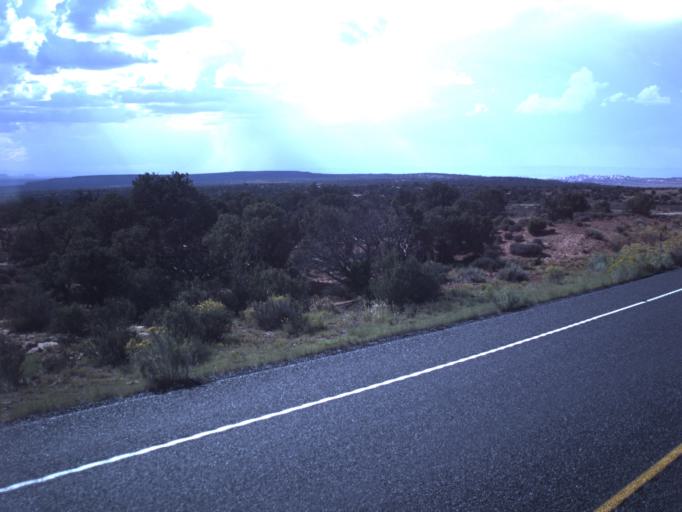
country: US
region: Utah
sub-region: Grand County
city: Moab
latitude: 38.5811
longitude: -109.7979
